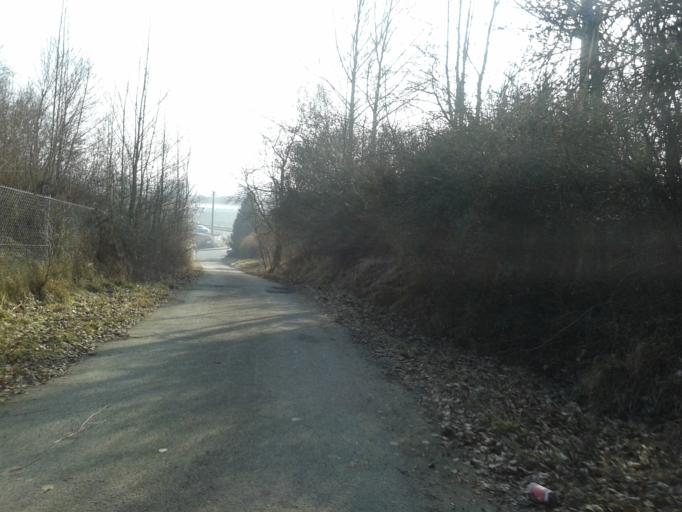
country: DE
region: Baden-Wuerttemberg
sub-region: Tuebingen Region
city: Ulm
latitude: 48.3756
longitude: 9.9538
